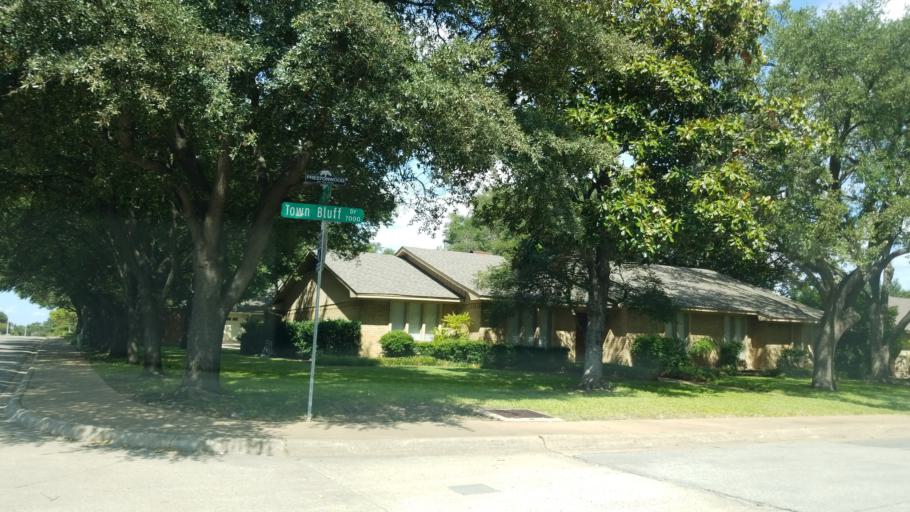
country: US
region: Texas
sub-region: Dallas County
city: Addison
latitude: 32.9553
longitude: -96.7867
